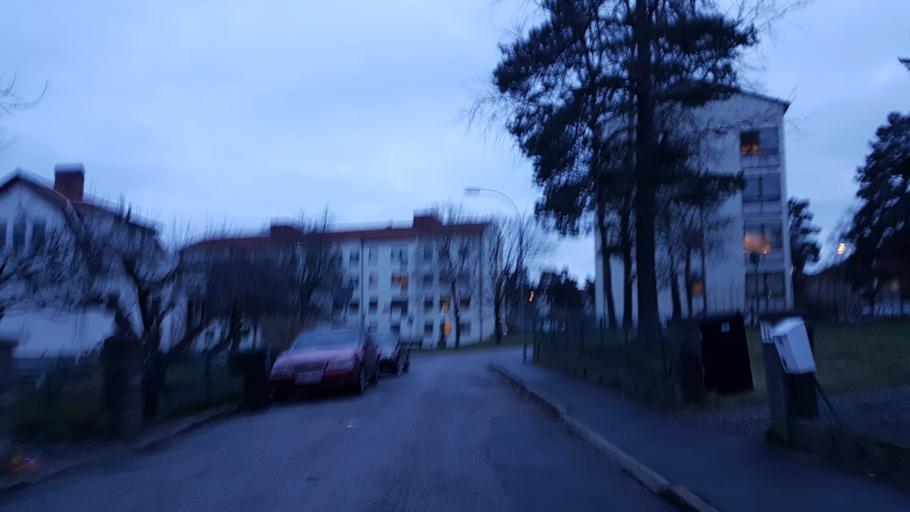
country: SE
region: Stockholm
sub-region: Stockholms Kommun
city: Arsta
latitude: 59.2754
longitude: 18.0522
